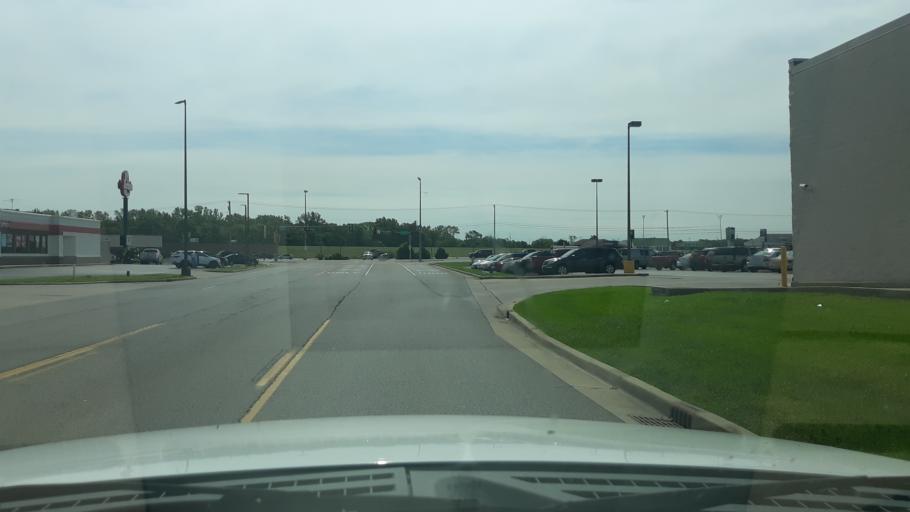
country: US
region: Illinois
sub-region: Saline County
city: Harrisburg
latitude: 37.7460
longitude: -88.5252
